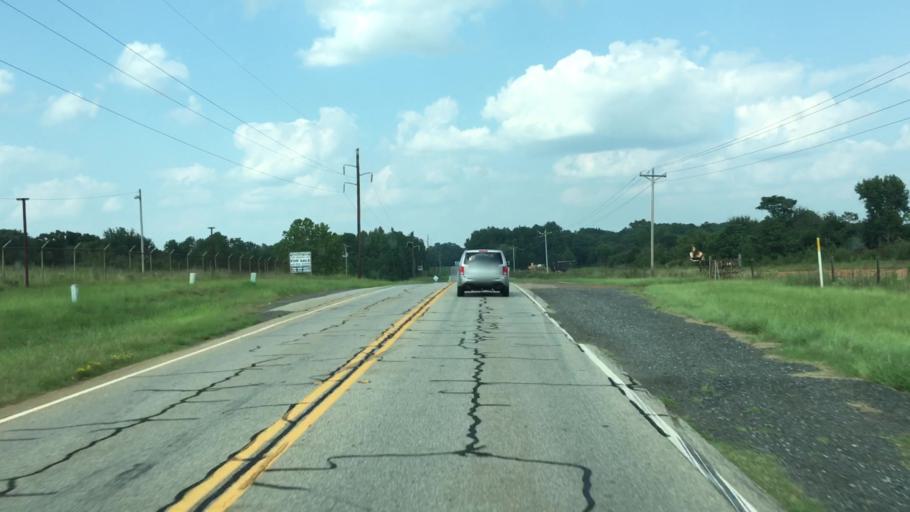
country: US
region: Georgia
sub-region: Jasper County
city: Monticello
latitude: 33.2873
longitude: -83.7094
